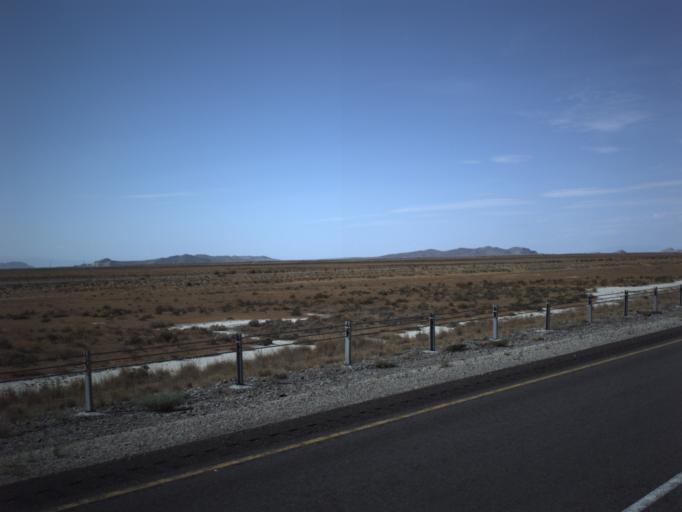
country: US
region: Utah
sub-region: Tooele County
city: Grantsville
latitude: 40.7262
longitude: -113.1610
